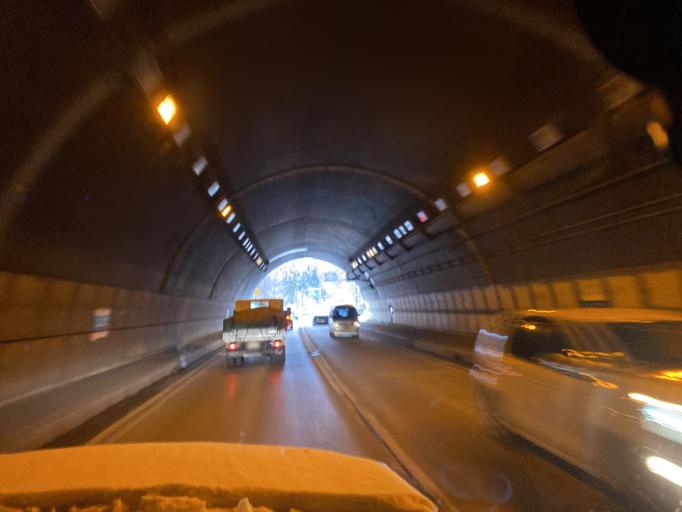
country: JP
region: Nagano
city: Nagano-shi
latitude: 36.6199
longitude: 138.1122
